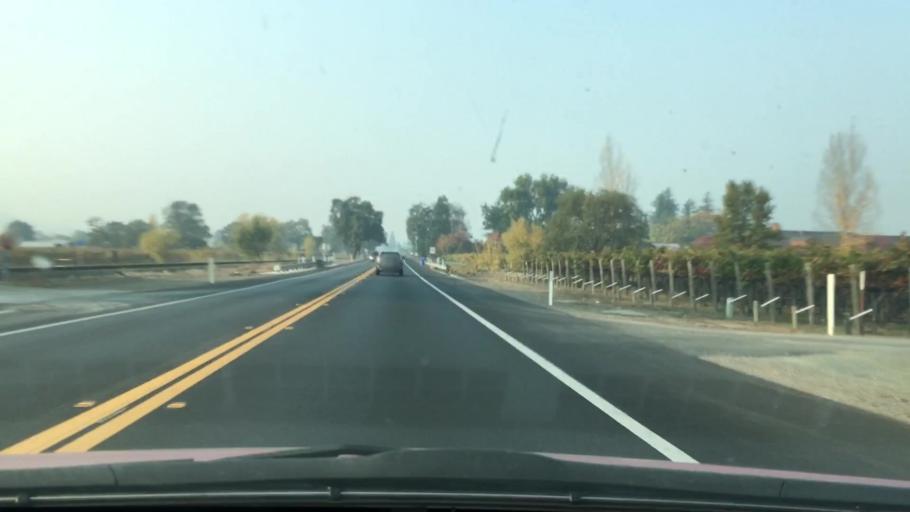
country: US
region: California
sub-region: Napa County
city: Yountville
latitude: 38.4452
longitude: -122.4104
